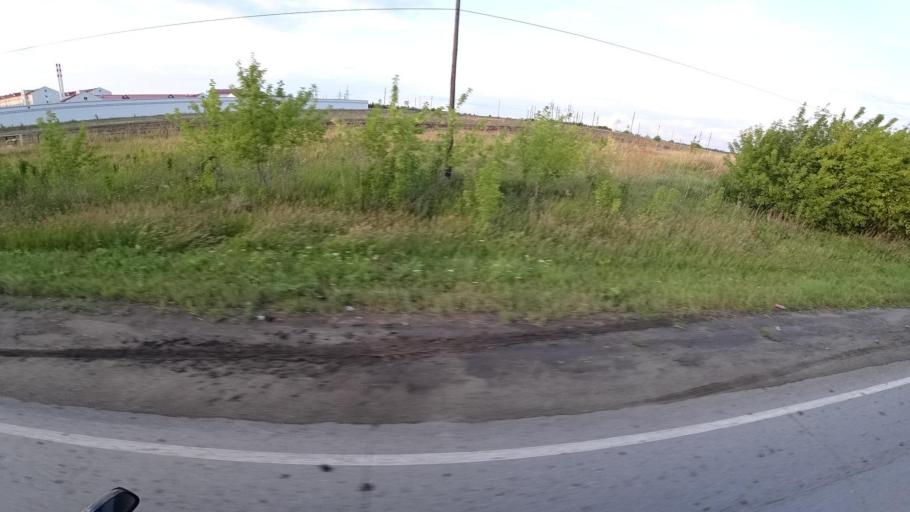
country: RU
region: Sverdlovsk
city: Kamyshlov
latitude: 56.8532
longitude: 62.7376
